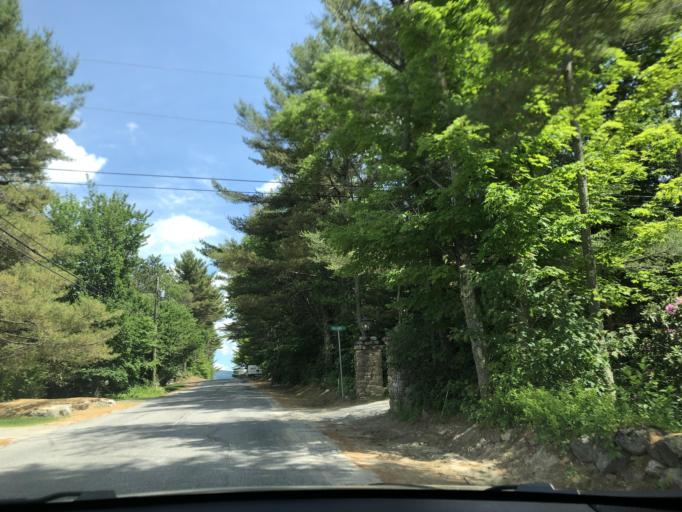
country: US
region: New Hampshire
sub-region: Merrimack County
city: New London
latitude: 43.4110
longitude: -72.0029
